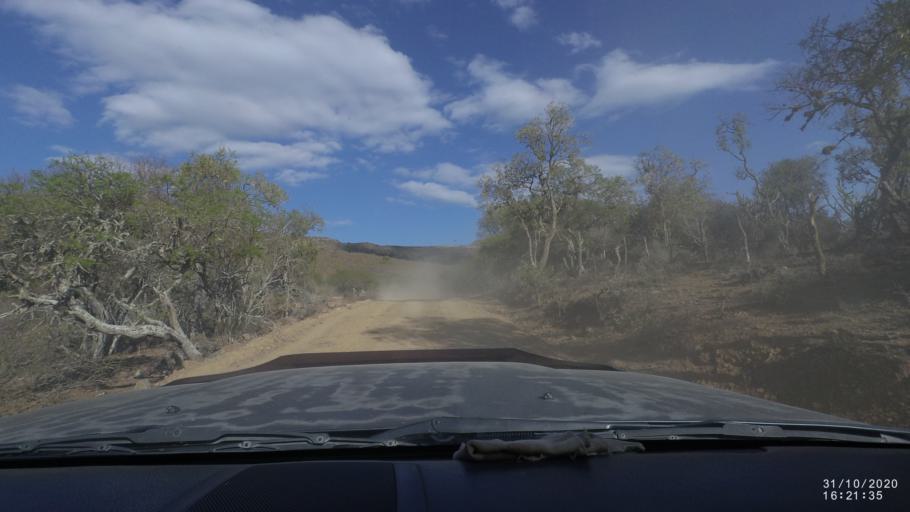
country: BO
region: Chuquisaca
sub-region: Provincia Zudanez
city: Mojocoya
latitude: -18.3991
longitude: -64.5969
